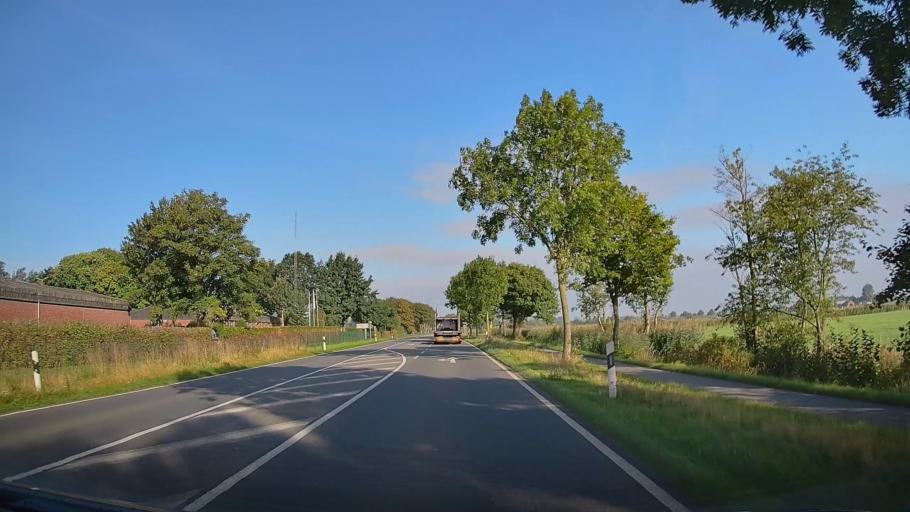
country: DE
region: Lower Saxony
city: Ovelgonne
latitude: 53.3446
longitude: 8.4475
